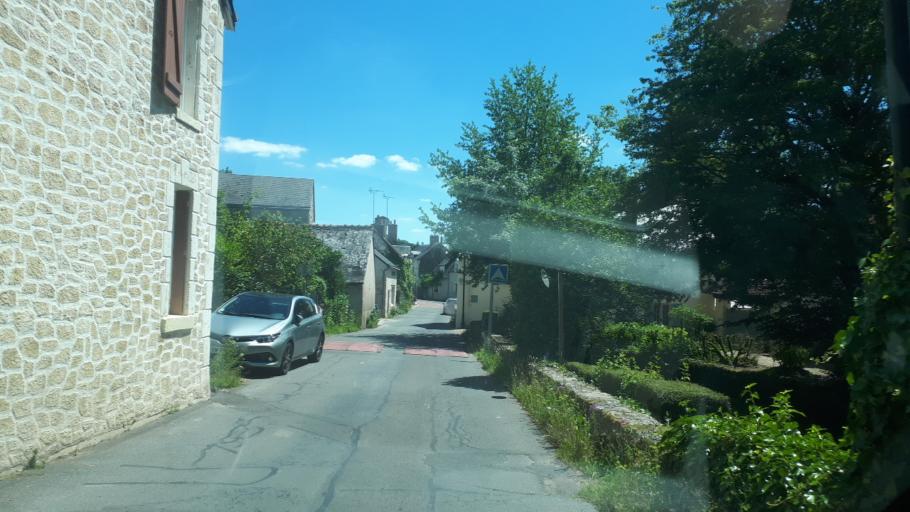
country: FR
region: Centre
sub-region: Departement du Loir-et-Cher
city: Saint-Sulpice-de-Pommeray
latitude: 47.5791
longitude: 1.2154
